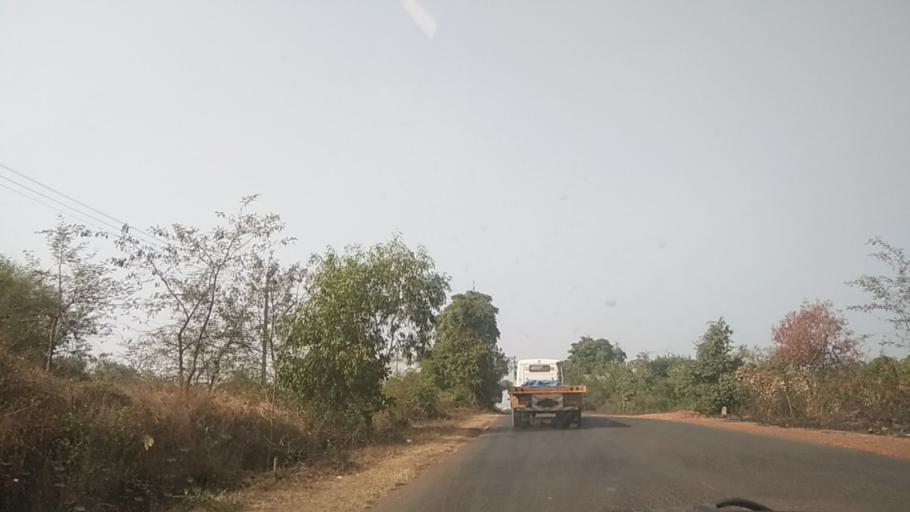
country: IN
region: Goa
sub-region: North Goa
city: Colovale
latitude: 15.6765
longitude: 73.8370
